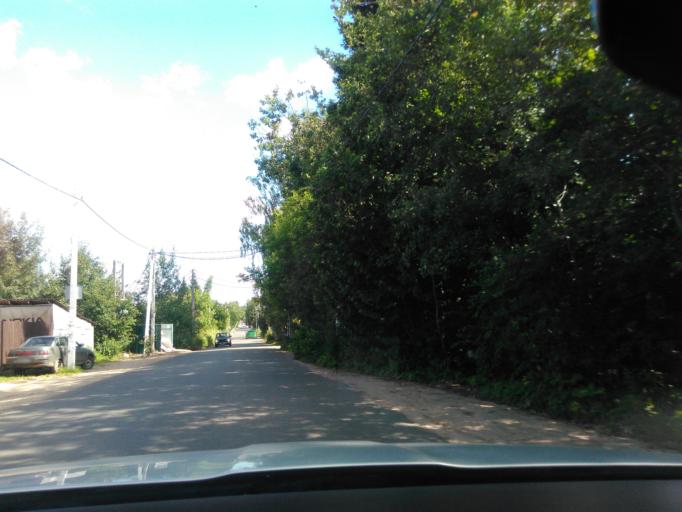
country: RU
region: Moskovskaya
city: Klin
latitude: 56.2326
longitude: 36.8200
